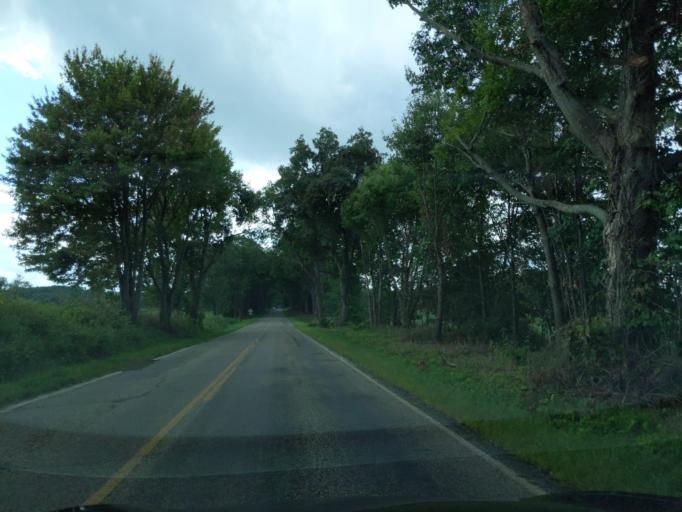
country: US
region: Michigan
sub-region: Eaton County
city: Eaton Rapids
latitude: 42.3787
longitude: -84.5918
